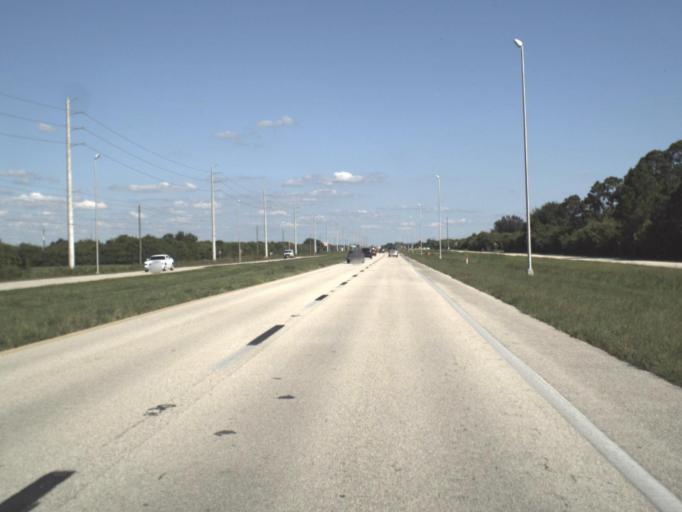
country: US
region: Florida
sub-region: Charlotte County
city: Rotonda
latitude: 26.9326
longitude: -82.2563
